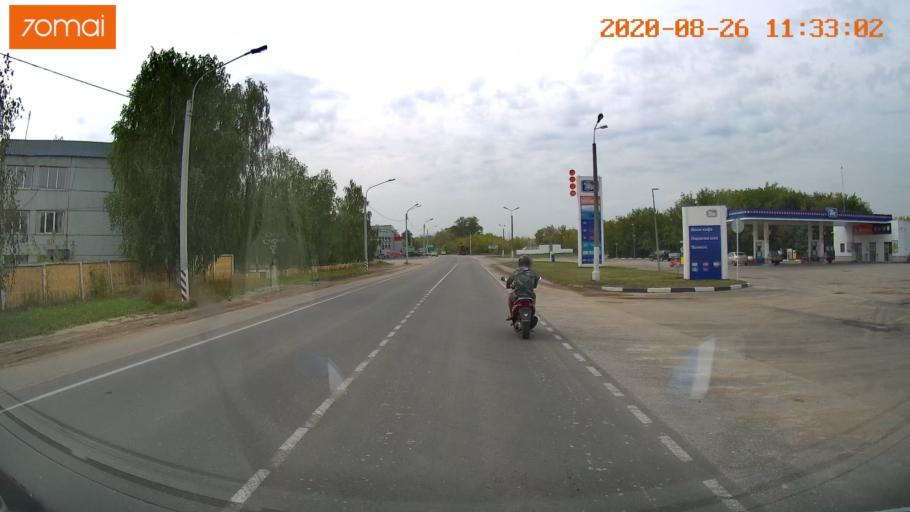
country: RU
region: Rjazan
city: Shilovo
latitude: 54.2988
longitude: 40.8584
